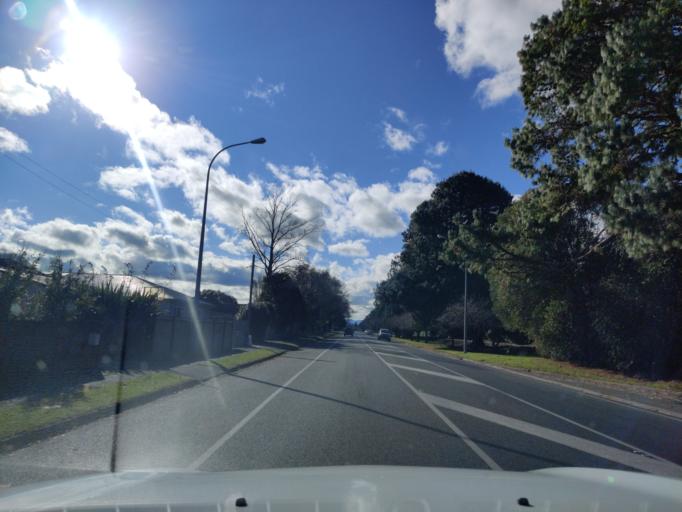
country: NZ
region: Waikato
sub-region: Matamata-Piako District
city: Matamata
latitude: -37.8205
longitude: 175.7711
